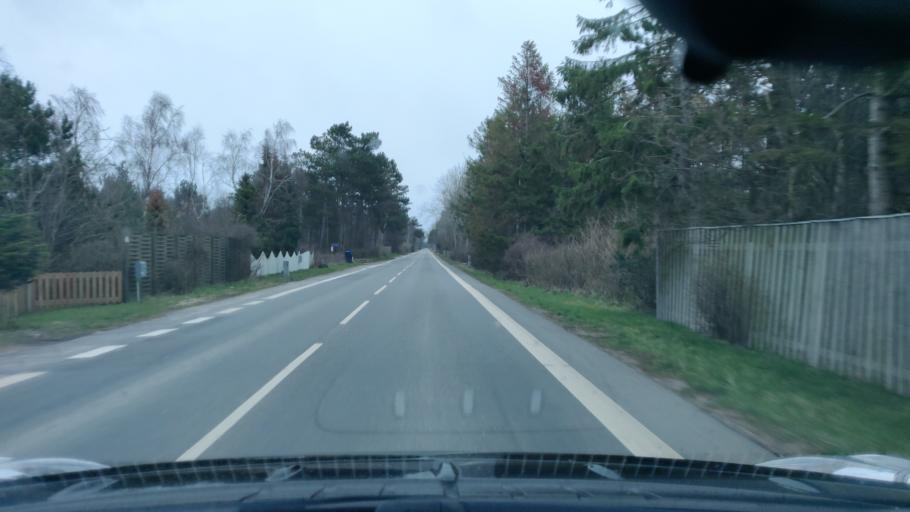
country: DK
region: Zealand
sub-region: Odsherred Kommune
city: Hojby
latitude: 55.8717
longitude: 11.5400
